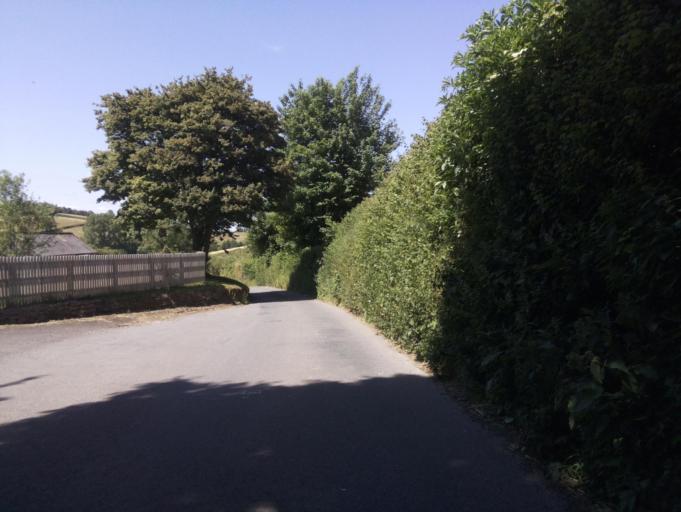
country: GB
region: England
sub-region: Devon
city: Marldon
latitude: 50.4624
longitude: -3.5948
